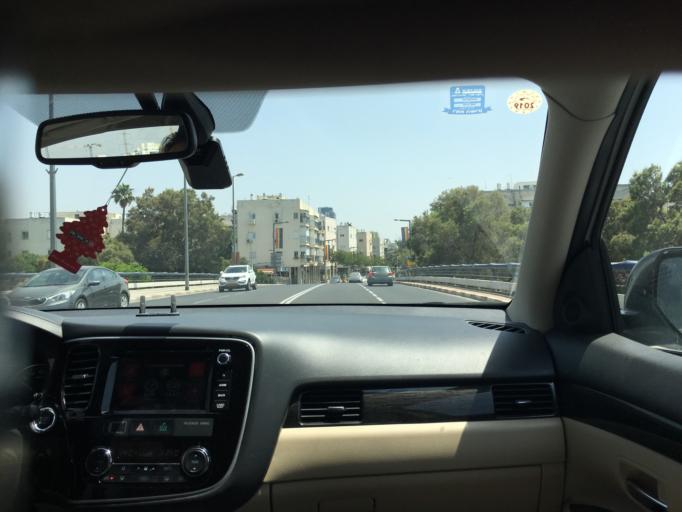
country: IL
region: Tel Aviv
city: Tel Aviv
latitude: 32.0962
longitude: 34.7837
